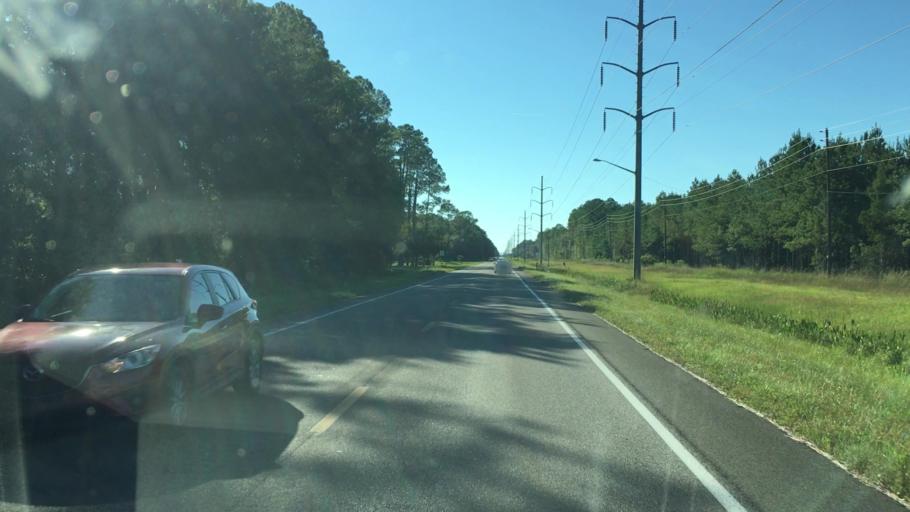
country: US
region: Florida
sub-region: Alachua County
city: Gainesville
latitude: 29.7032
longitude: -82.3281
